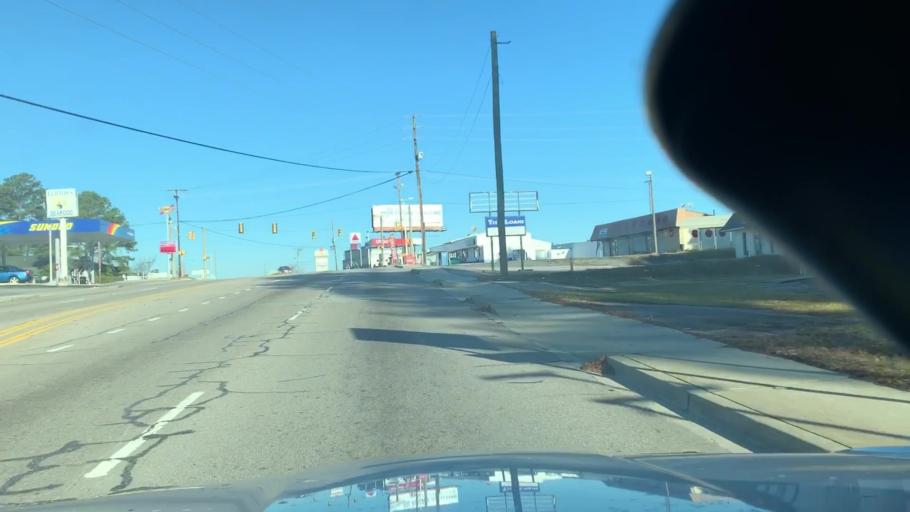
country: US
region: South Carolina
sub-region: Richland County
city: Woodfield
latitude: 34.0510
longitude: -80.9448
